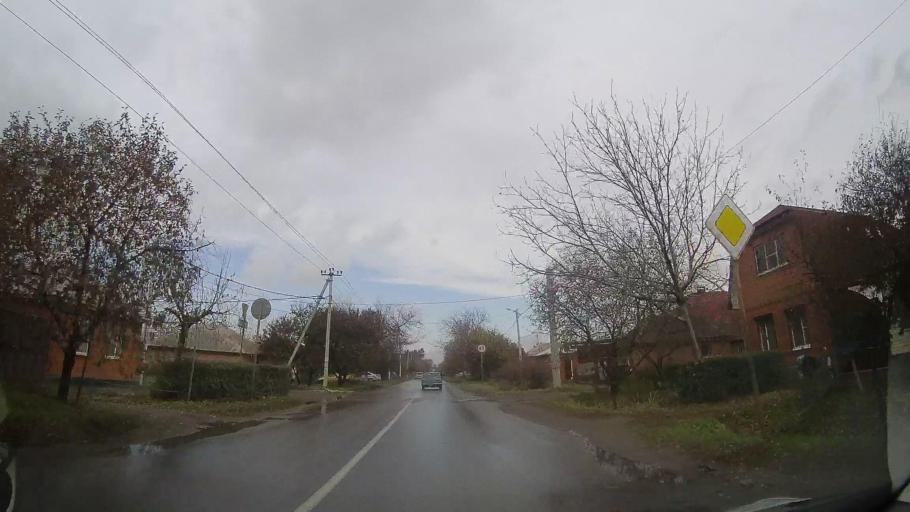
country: RU
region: Rostov
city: Bataysk
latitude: 47.1276
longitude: 39.7682
